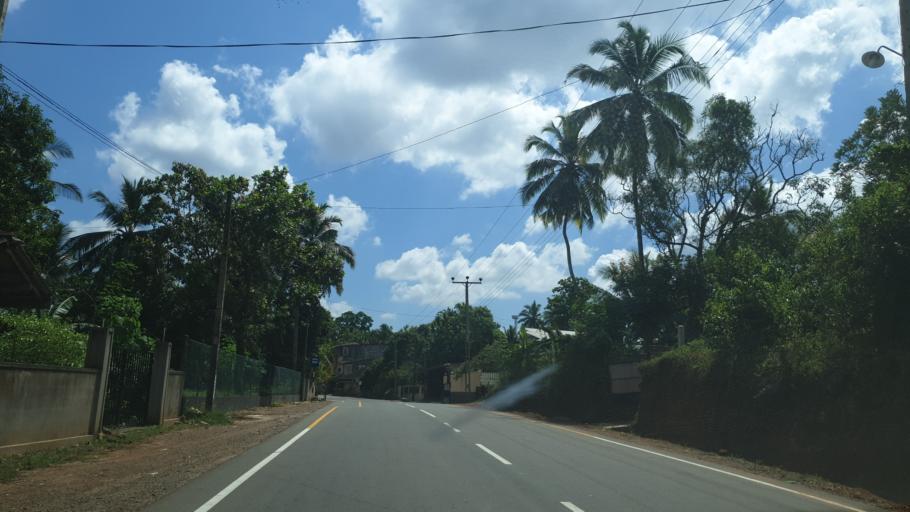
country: LK
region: Western
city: Kalutara
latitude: 6.6645
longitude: 79.9690
